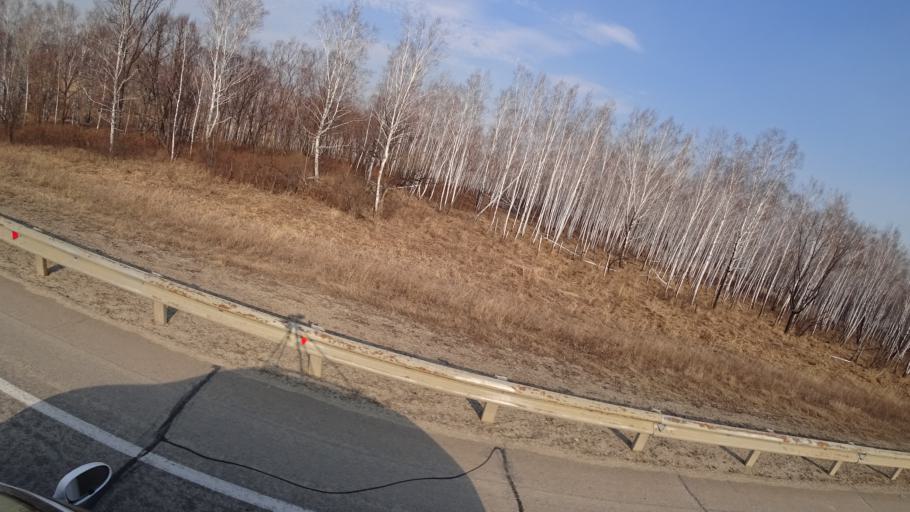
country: RU
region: Amur
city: Novobureyskiy
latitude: 49.8508
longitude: 129.8869
